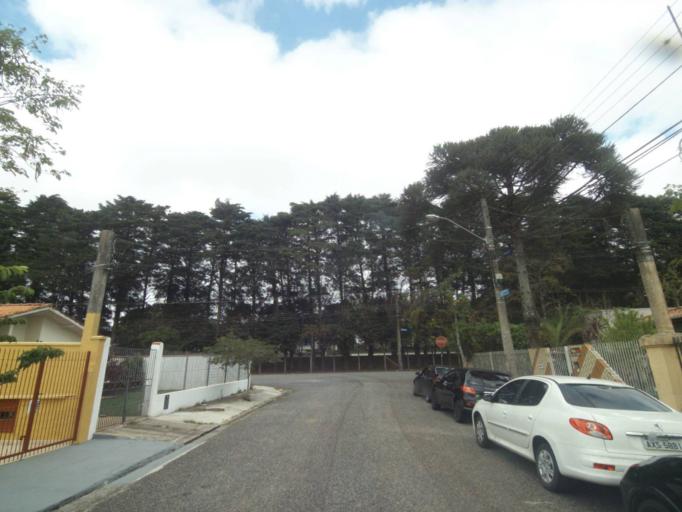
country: BR
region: Parana
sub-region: Curitiba
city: Curitiba
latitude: -25.3961
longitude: -49.2252
